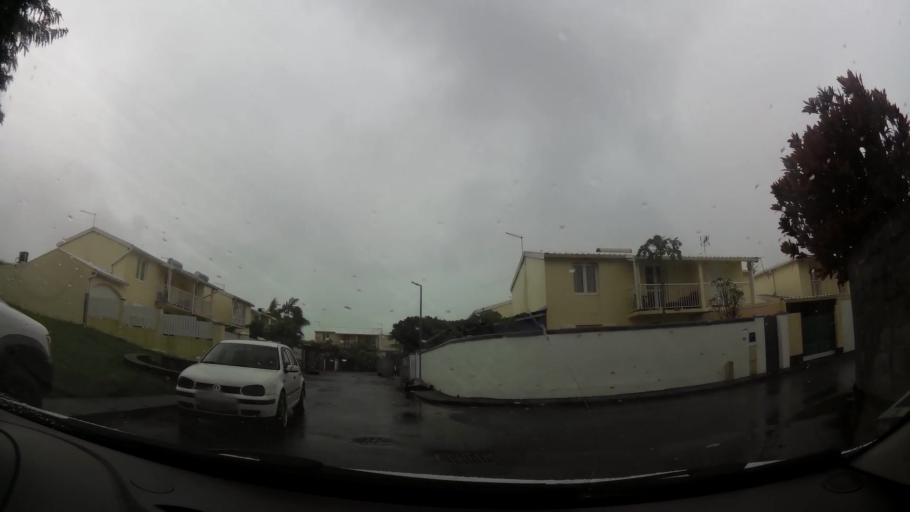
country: RE
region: Reunion
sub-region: Reunion
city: Saint-Andre
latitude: -20.9632
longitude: 55.6434
